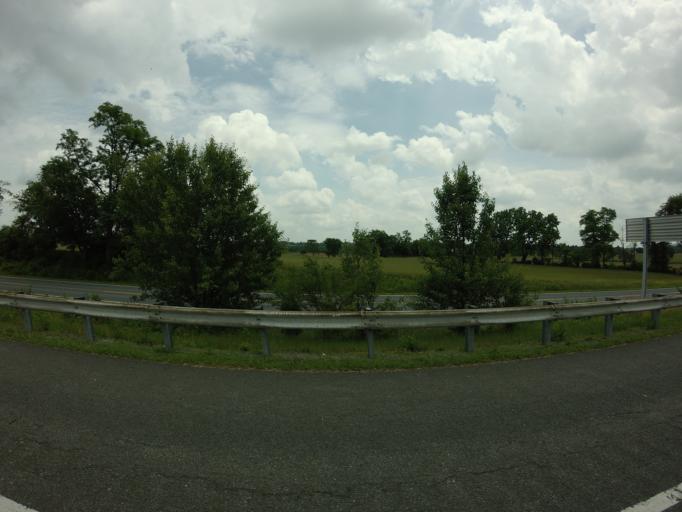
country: US
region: Maryland
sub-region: Frederick County
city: Ballenger Creek
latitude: 39.3750
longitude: -77.4791
